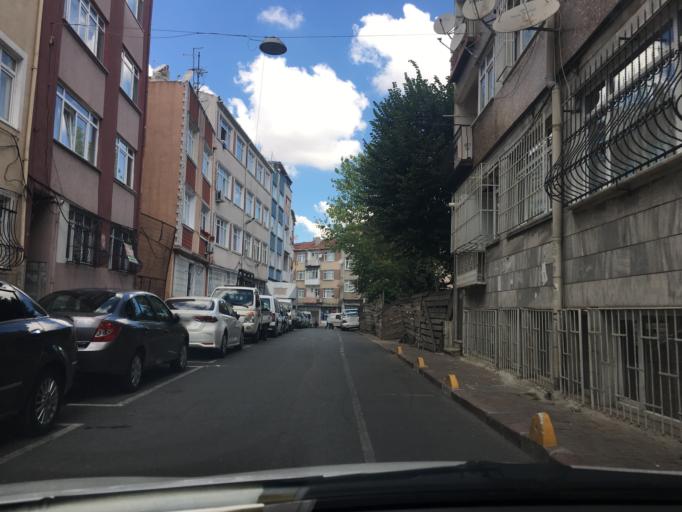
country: TR
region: Istanbul
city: Istanbul
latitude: 41.0115
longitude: 28.9294
